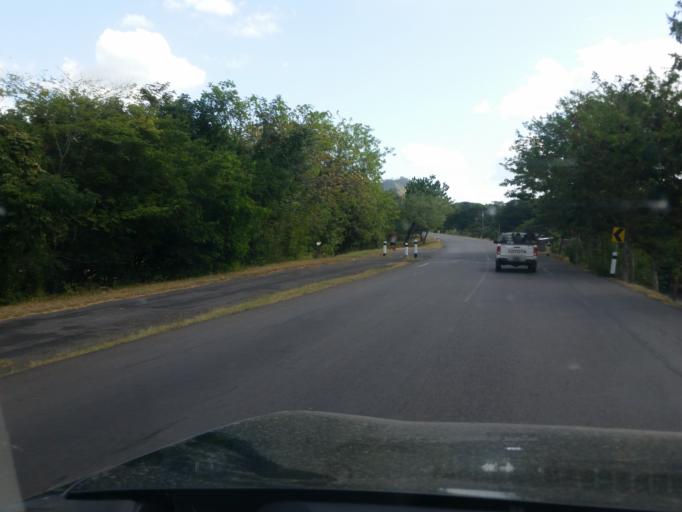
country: NI
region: Chontales
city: Comalapa
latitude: 12.1914
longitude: -85.6136
